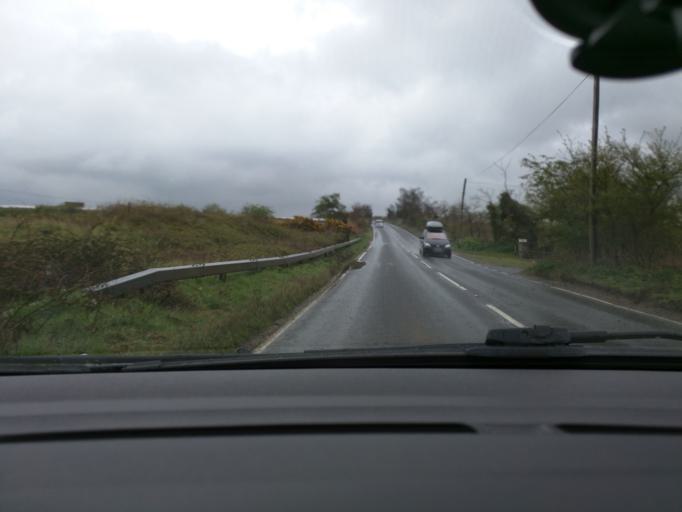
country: GB
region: England
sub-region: Suffolk
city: Saxmundham
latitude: 52.1799
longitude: 1.5250
